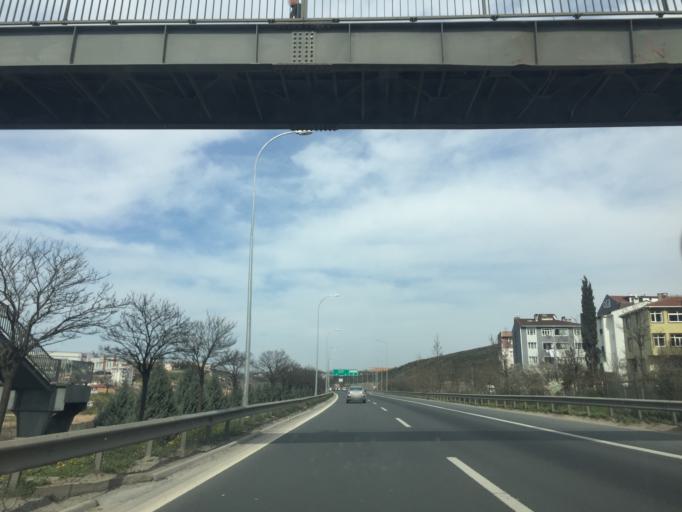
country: TR
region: Kocaeli
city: Darica
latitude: 40.8350
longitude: 29.3712
